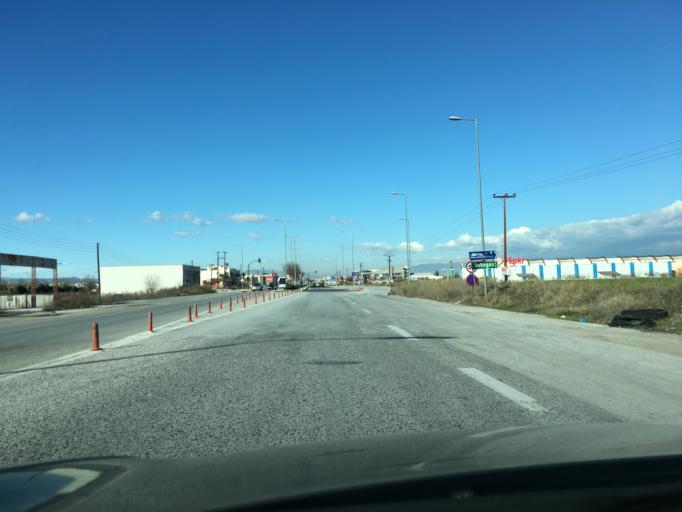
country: GR
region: Thessaly
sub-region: Nomos Larisis
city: Larisa
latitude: 39.6033
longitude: 22.4428
